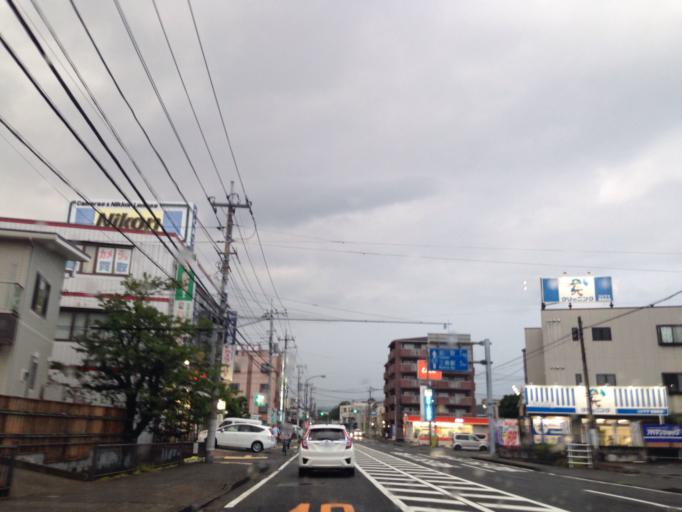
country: JP
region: Shizuoka
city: Mishima
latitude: 35.1128
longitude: 138.9149
